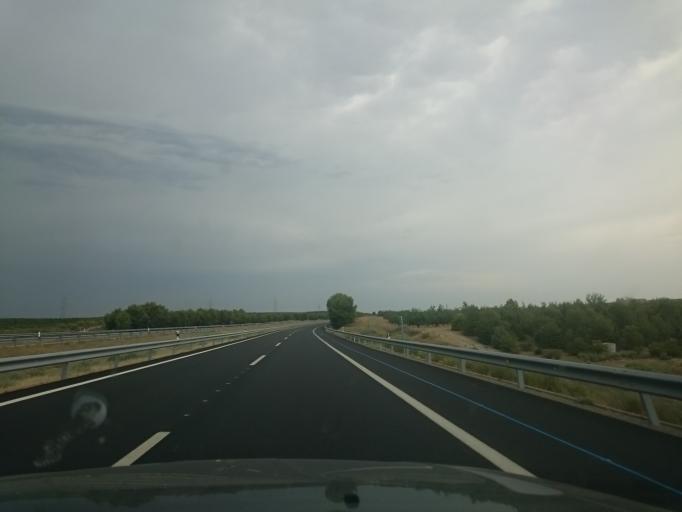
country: ES
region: Aragon
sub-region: Provincia de Zaragoza
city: Pina de Ebro
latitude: 41.5376
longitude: -0.5251
